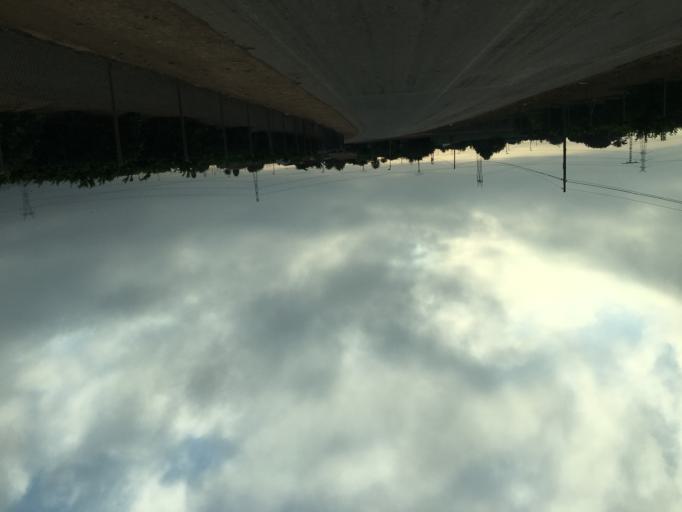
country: ES
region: Murcia
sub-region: Murcia
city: Cartagena
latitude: 37.6626
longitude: -0.9390
